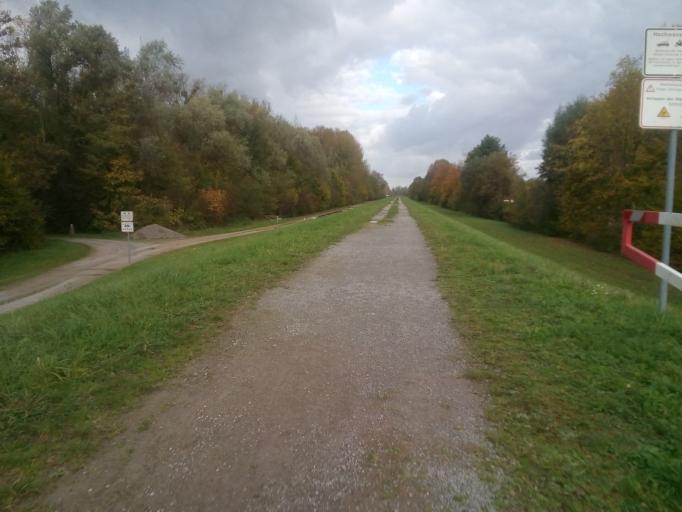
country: DE
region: Baden-Wuerttemberg
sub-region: Karlsruhe Region
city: Schwarzach
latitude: 48.7732
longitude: 8.0329
